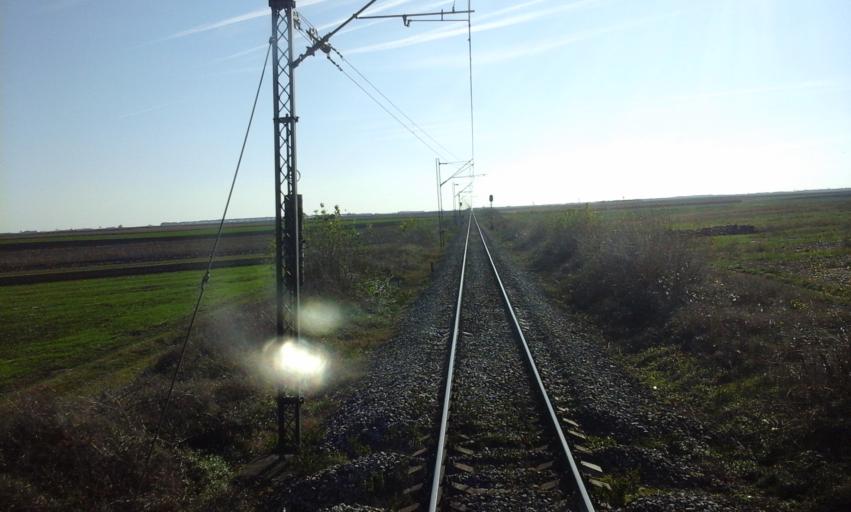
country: RS
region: Autonomna Pokrajina Vojvodina
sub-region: Severnobacki Okrug
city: Backa Topola
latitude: 45.9187
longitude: 19.6650
